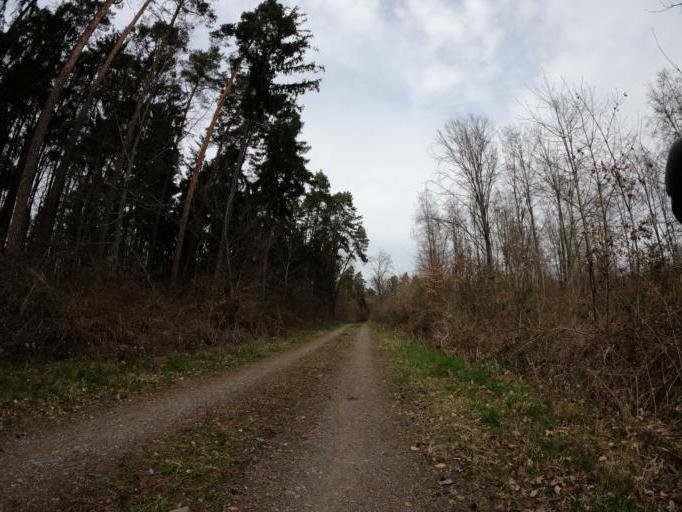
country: DE
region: Baden-Wuerttemberg
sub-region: Regierungsbezirk Stuttgart
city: Filderstadt
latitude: 48.6394
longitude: 9.1827
